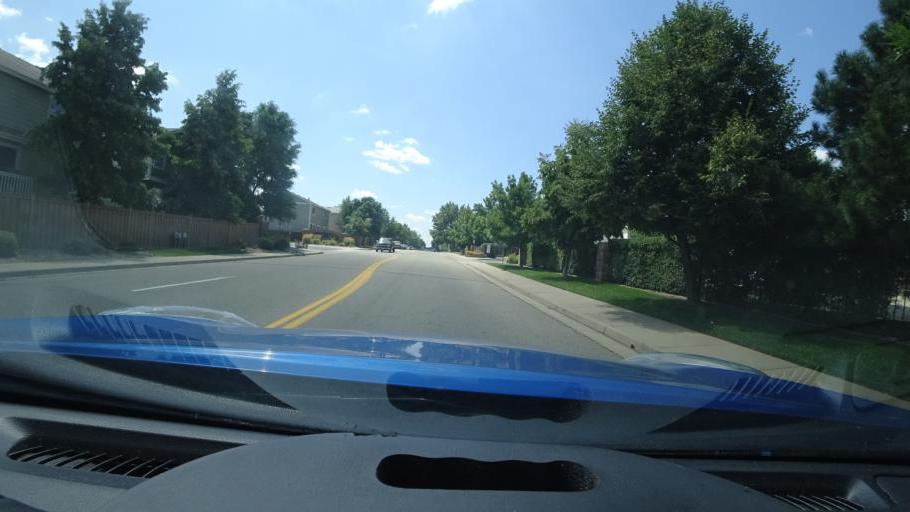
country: US
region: Colorado
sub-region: Arapahoe County
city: Glendale
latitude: 39.6957
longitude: -104.8823
